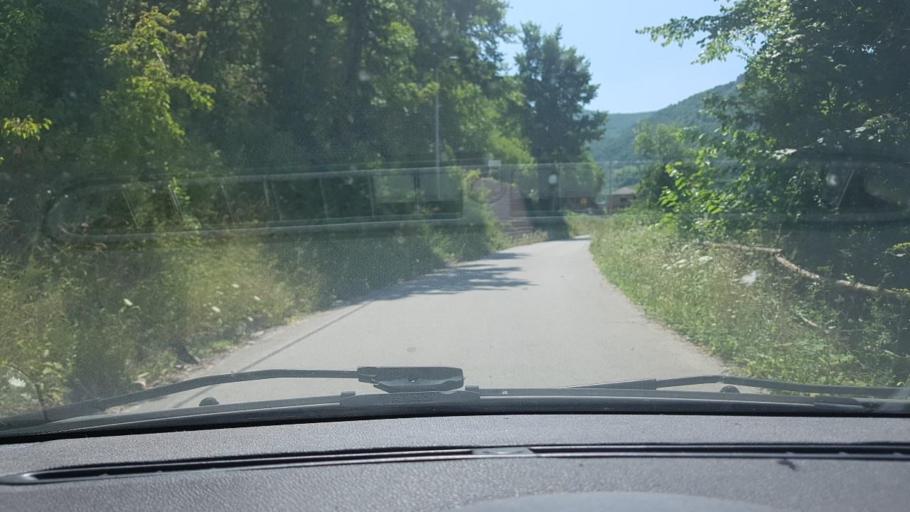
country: BA
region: Federation of Bosnia and Herzegovina
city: Orasac
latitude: 44.5689
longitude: 16.0840
